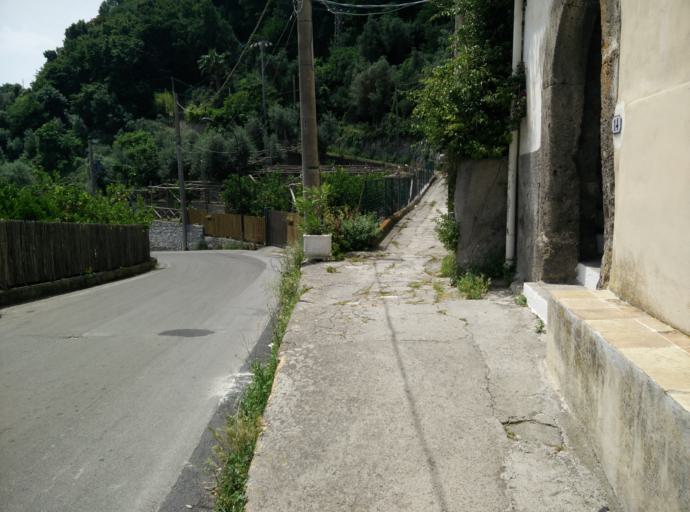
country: IT
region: Campania
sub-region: Provincia di Napoli
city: Massa Lubrense
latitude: 40.5859
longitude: 14.3470
